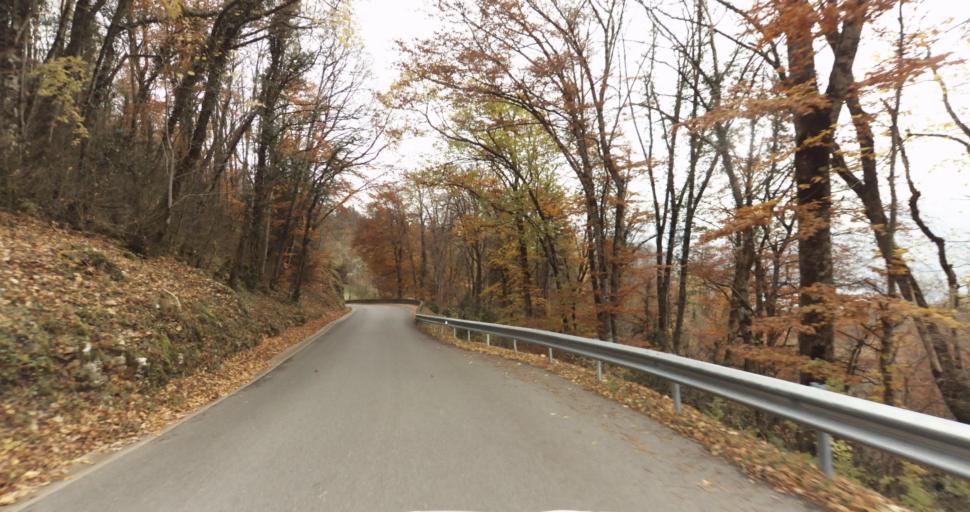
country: FR
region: Rhone-Alpes
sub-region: Departement de la Haute-Savoie
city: Talloires
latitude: 45.8156
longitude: 6.1957
